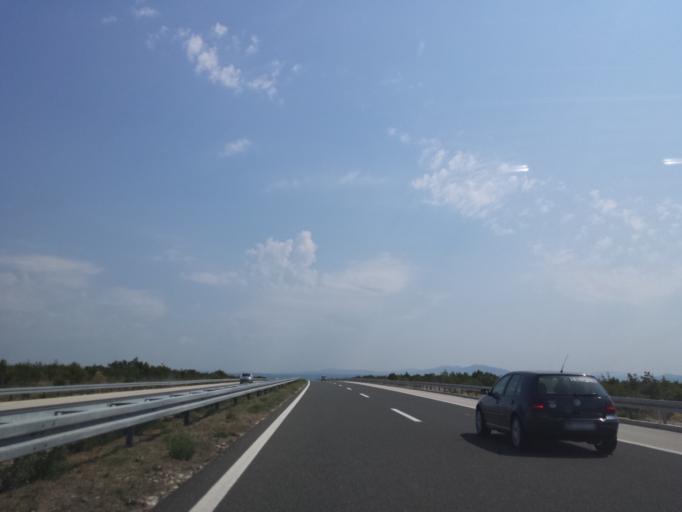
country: HR
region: Sibensko-Kniniska
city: Zaton
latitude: 43.8632
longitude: 15.8211
